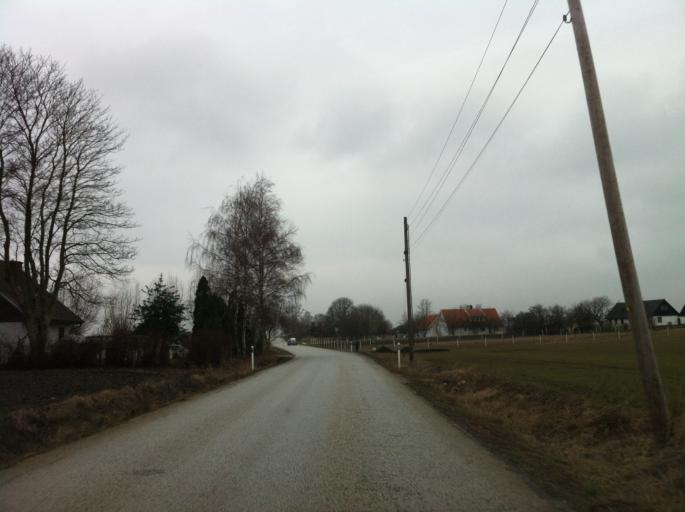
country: SE
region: Skane
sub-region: Svalovs Kommun
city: Svaloev
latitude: 55.9458
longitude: 13.0305
